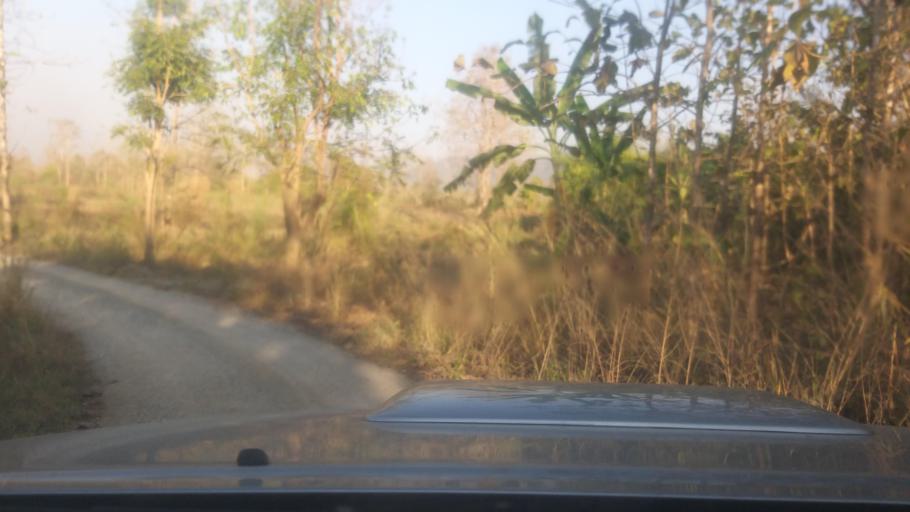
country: TH
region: Phrae
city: Nong Muang Khai
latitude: 18.2670
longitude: 100.0226
